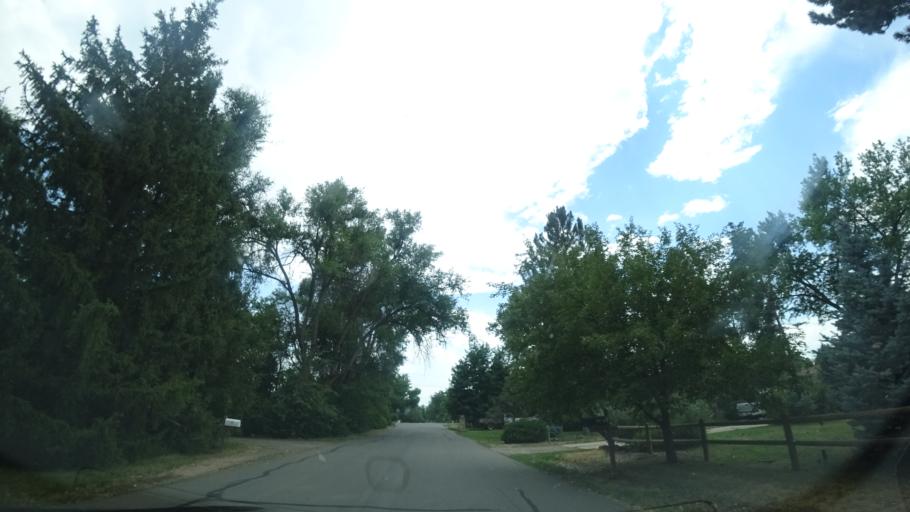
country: US
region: Colorado
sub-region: Jefferson County
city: Lakewood
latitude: 39.7191
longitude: -105.1016
